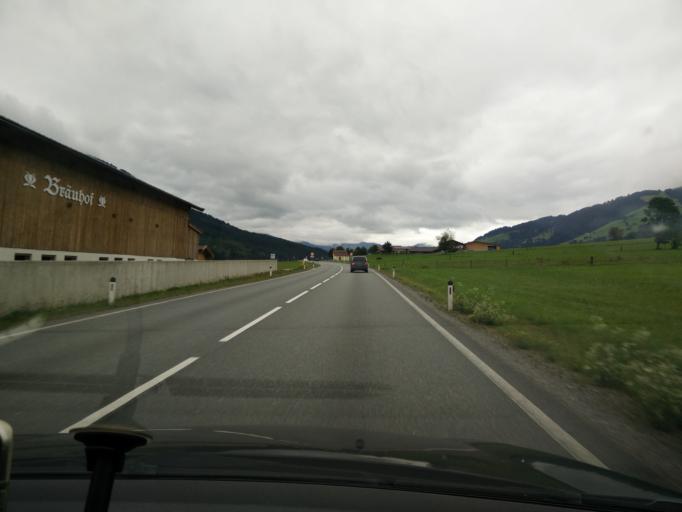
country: AT
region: Tyrol
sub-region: Politischer Bezirk Kitzbuhel
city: Kirchberg in Tirol
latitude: 47.4523
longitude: 12.2837
